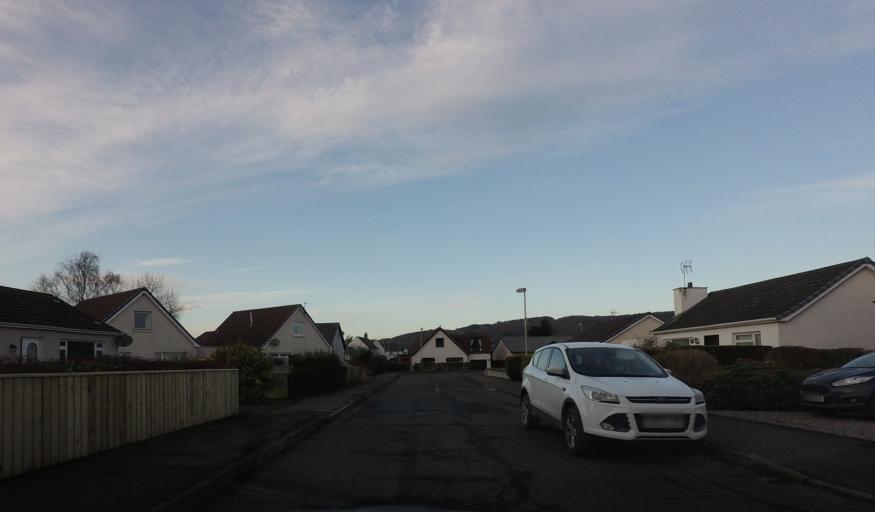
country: GB
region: Scotland
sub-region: Perth and Kinross
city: Bridge of Earn
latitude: 56.3405
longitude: -3.4050
